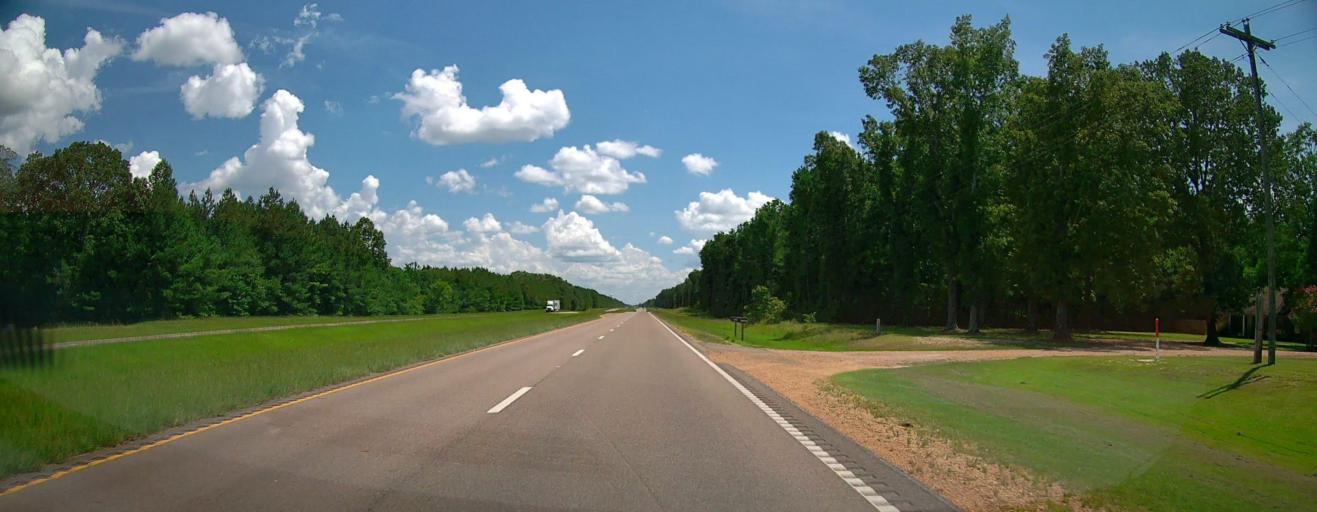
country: US
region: Mississippi
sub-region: Monroe County
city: Aberdeen
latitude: 33.9219
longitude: -88.5962
